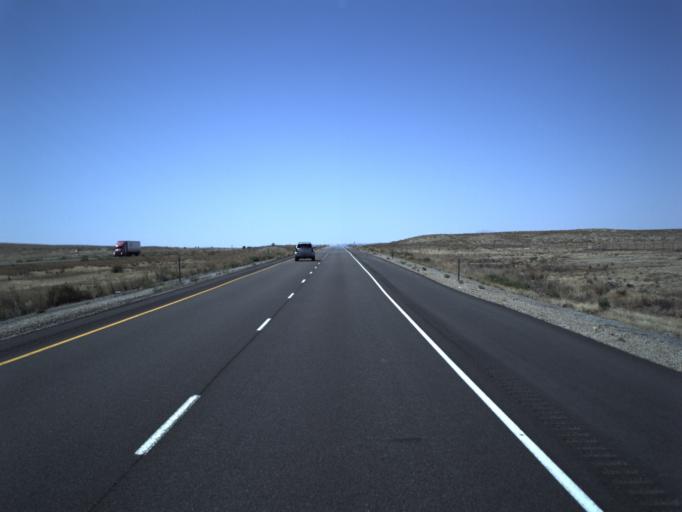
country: US
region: Colorado
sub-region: Mesa County
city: Loma
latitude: 39.0982
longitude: -109.2044
